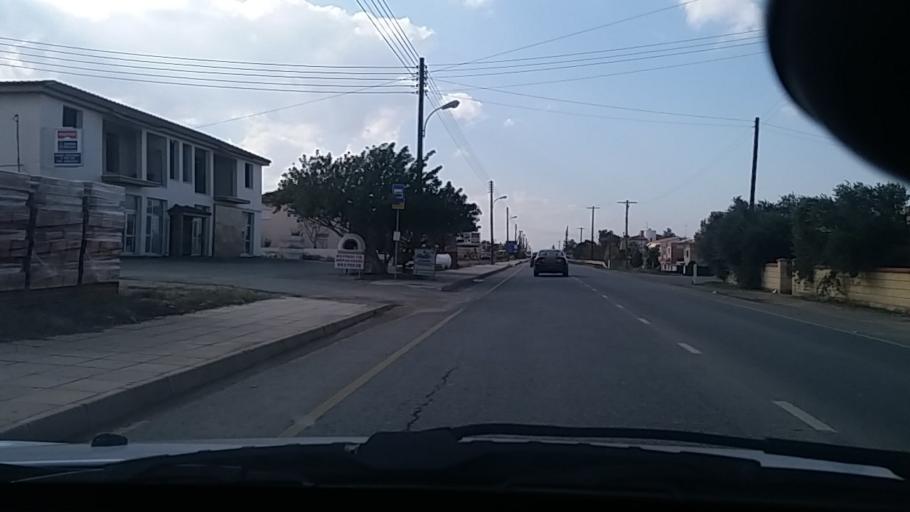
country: CY
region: Lefkosia
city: Akaki
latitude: 35.1373
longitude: 33.1456
